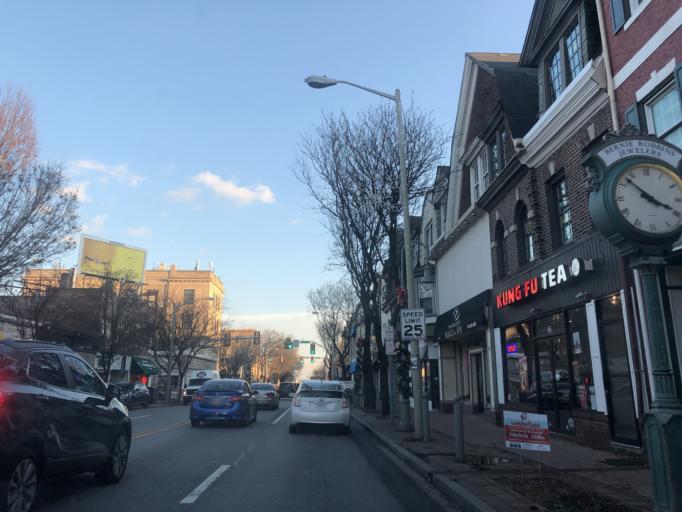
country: US
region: Pennsylvania
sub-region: Montgomery County
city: Ardmore
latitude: 40.0084
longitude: -75.2920
